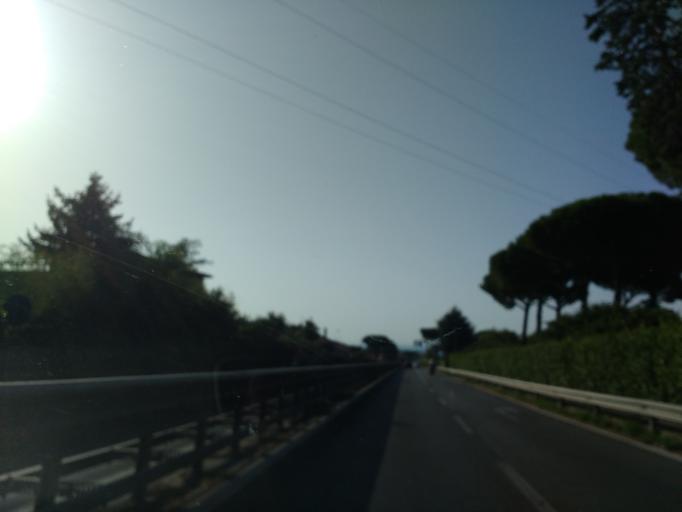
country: IT
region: Latium
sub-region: Citta metropolitana di Roma Capitale
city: Marino
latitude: 41.7607
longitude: 12.6231
